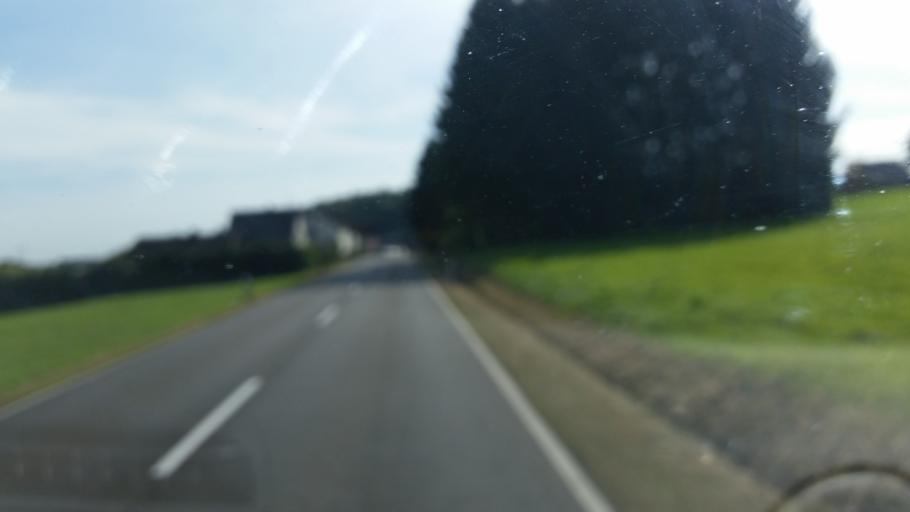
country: DE
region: Rheinland-Pfalz
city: Brandscheid
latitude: 50.5685
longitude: 7.9054
